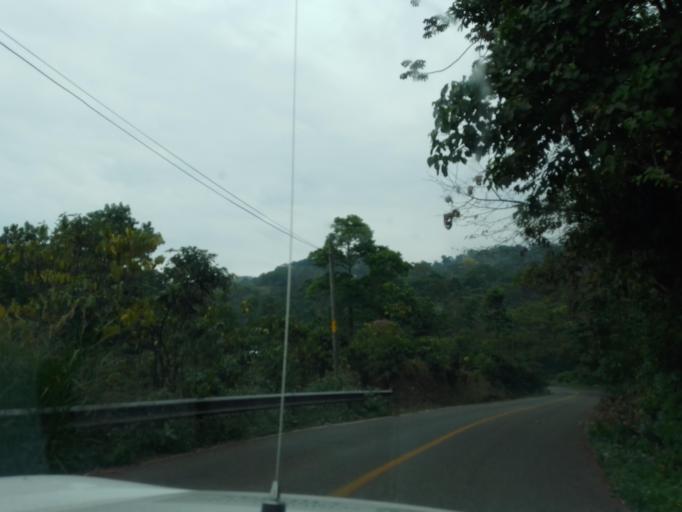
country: MX
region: Chiapas
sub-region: Union Juarez
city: Santo Domingo
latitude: 15.0369
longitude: -92.1216
